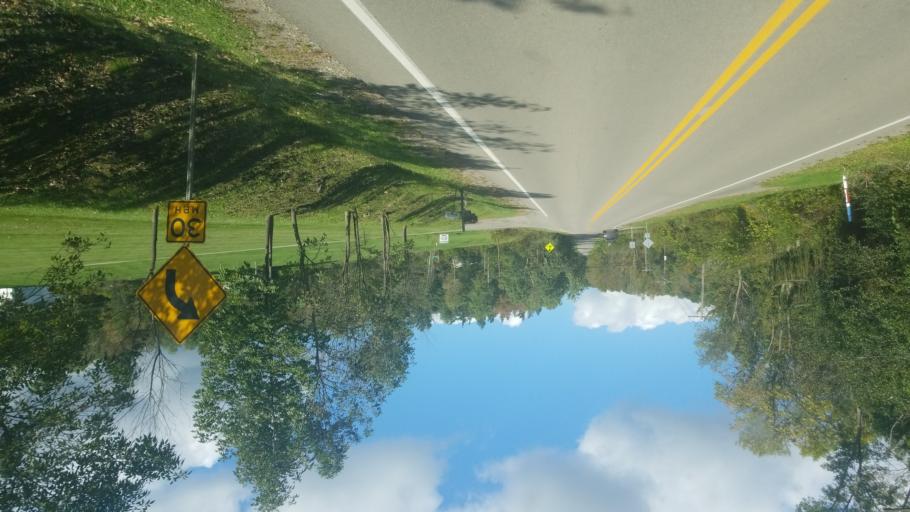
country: US
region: New York
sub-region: Allegany County
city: Cuba
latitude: 42.2519
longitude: -78.2770
